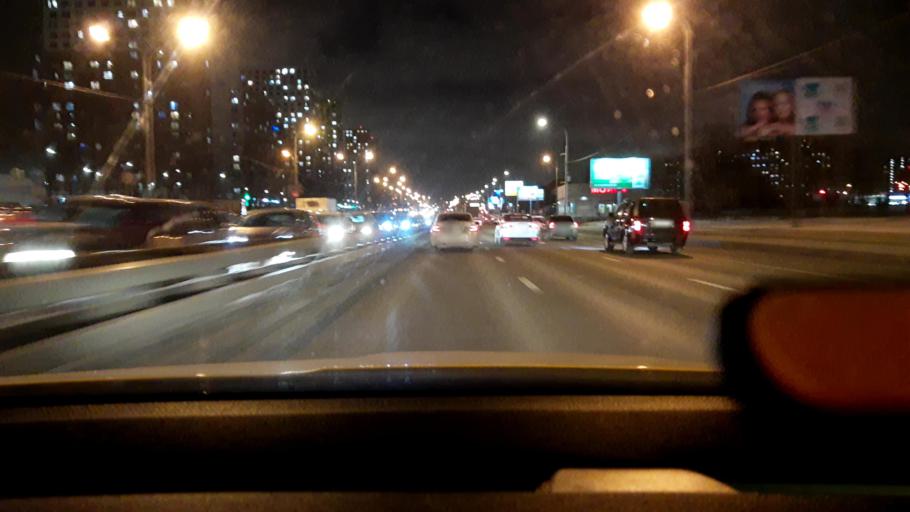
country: RU
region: Moscow
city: Mikhalkovo
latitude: 55.6626
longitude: 37.4168
